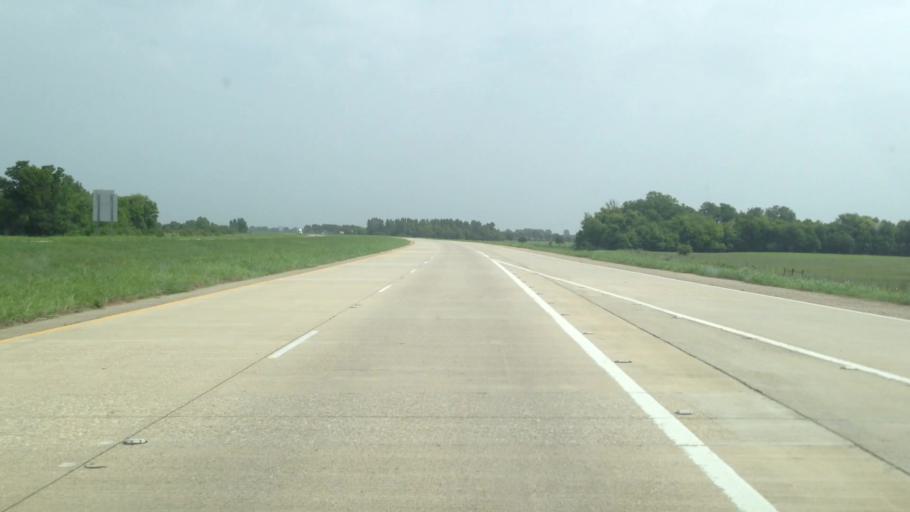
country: US
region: Louisiana
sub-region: Caddo Parish
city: Vivian
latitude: 32.8563
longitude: -93.8621
